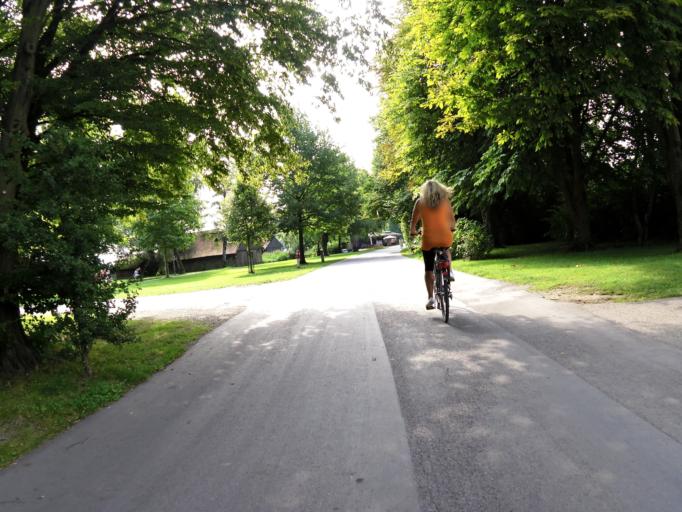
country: DE
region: Bavaria
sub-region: Upper Bavaria
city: Diessen am Ammersee
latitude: 47.9511
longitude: 11.1077
